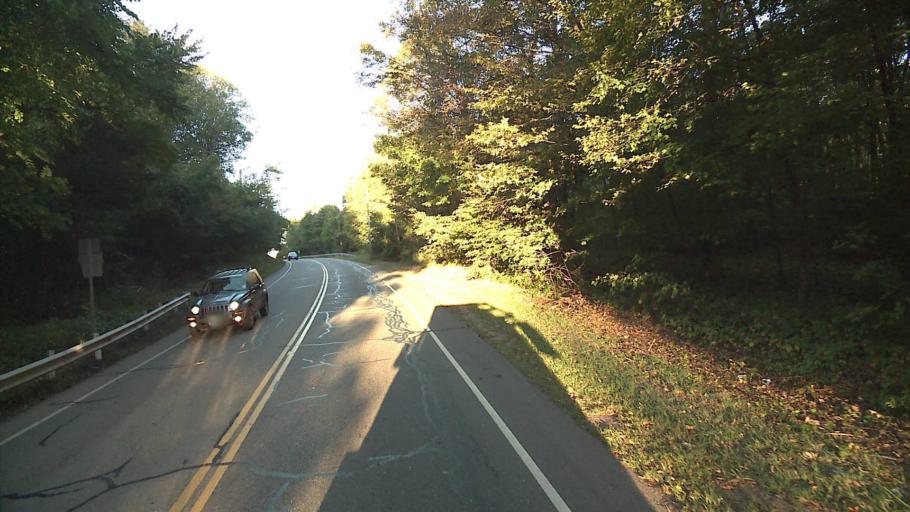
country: US
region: Connecticut
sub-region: Middlesex County
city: Durham
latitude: 41.4747
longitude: -72.7302
